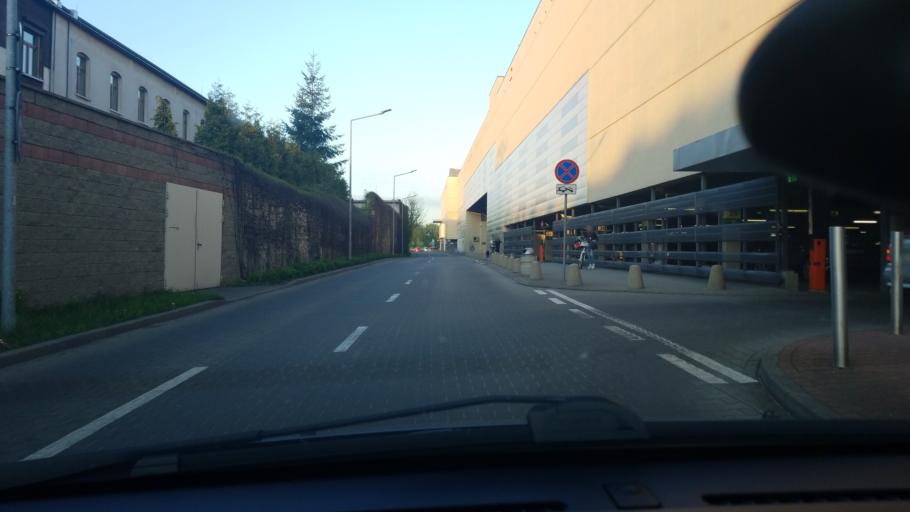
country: PL
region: Silesian Voivodeship
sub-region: Czestochowa
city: Czestochowa
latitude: 50.8085
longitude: 19.1295
